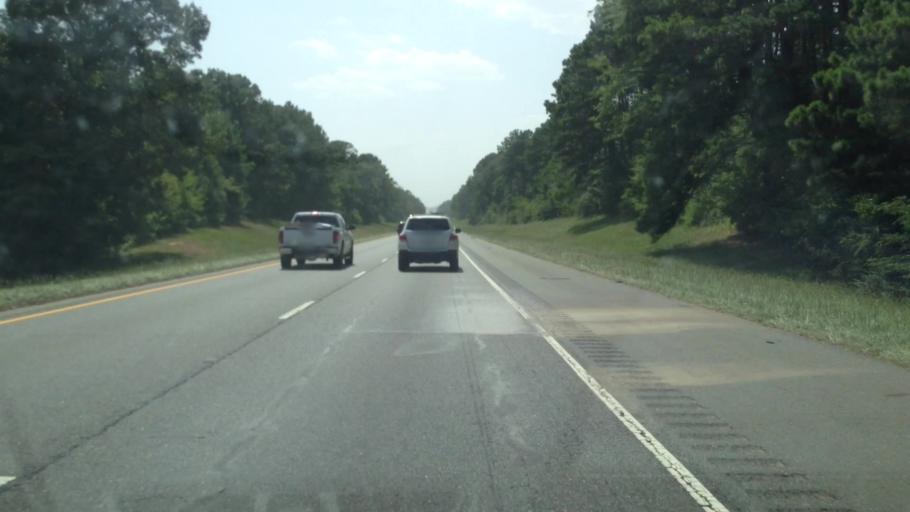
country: US
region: Louisiana
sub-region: Bossier Parish
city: Eastwood
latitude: 32.5423
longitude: -93.5538
